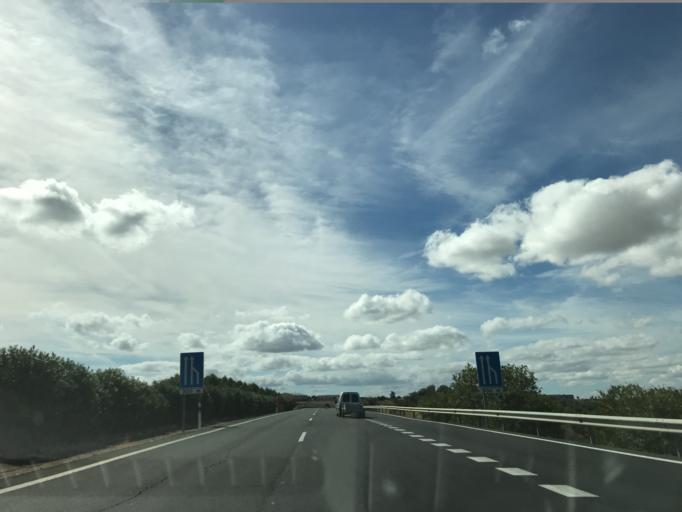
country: ES
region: Andalusia
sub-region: Province of Cordoba
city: La Victoria
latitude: 37.7212
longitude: -4.8613
